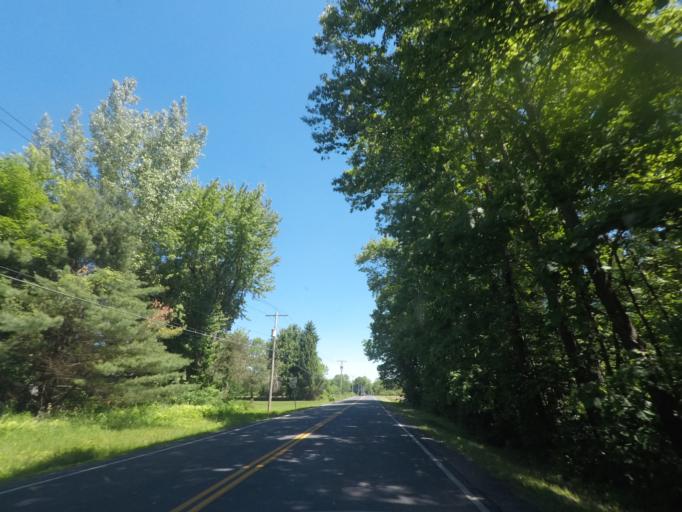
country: US
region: New York
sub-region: Saratoga County
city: Country Knolls
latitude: 42.8940
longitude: -73.8498
